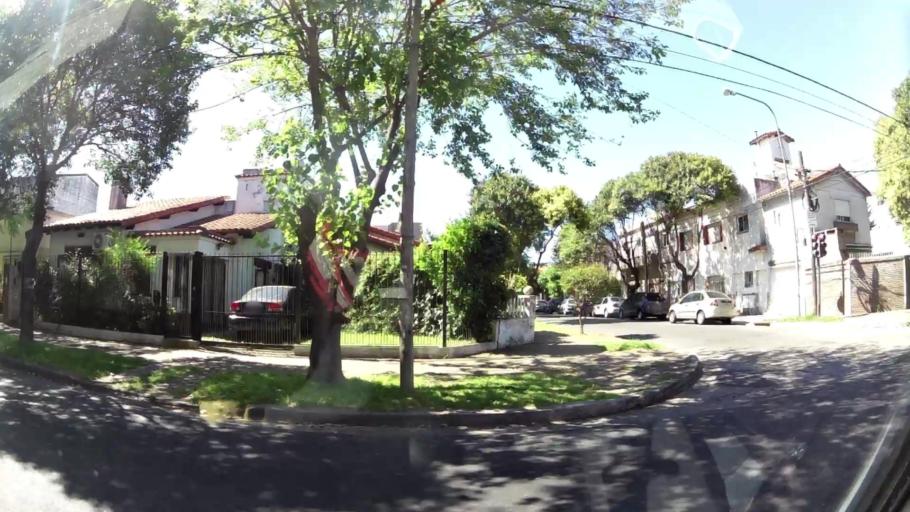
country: AR
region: Buenos Aires
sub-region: Partido de Vicente Lopez
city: Olivos
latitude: -34.5300
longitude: -58.5038
